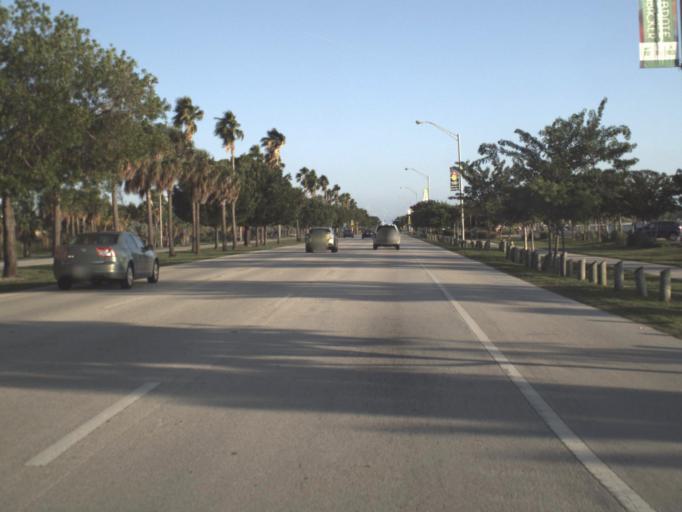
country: US
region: Florida
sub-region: Miami-Dade County
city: Miami
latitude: 25.7408
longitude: -80.1705
